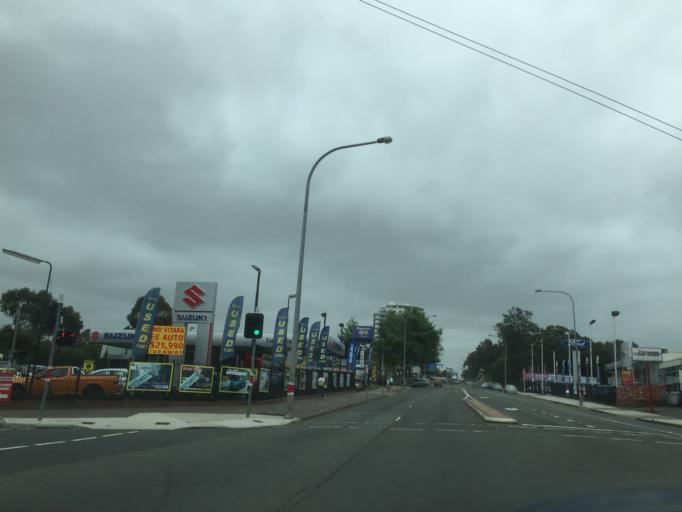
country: AU
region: New South Wales
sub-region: Blacktown
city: Blacktown
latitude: -33.7736
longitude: 150.9149
